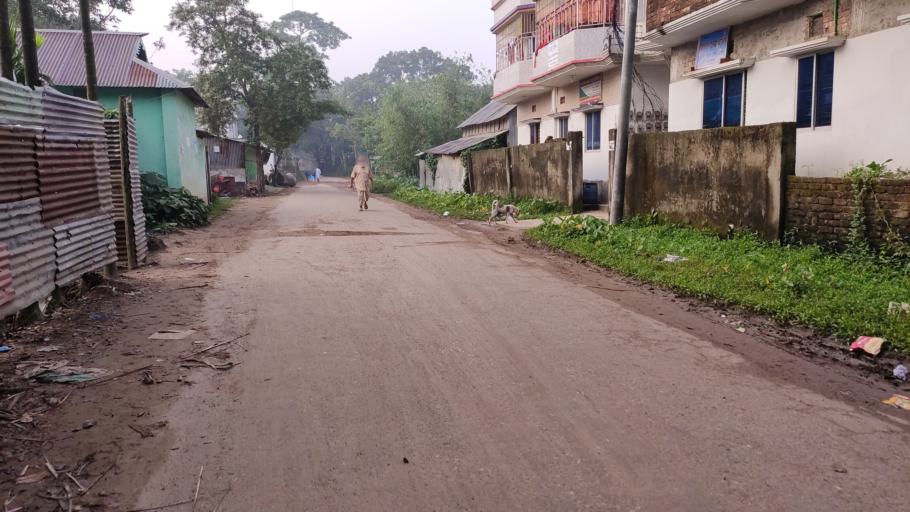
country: BD
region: Dhaka
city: Netrakona
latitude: 24.7139
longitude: 90.9468
